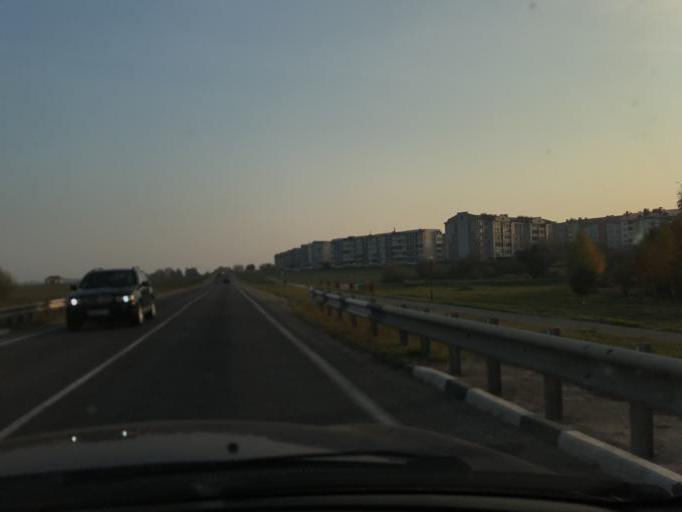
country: BY
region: Grodnenskaya
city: Karelichy
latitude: 53.5652
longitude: 26.1488
